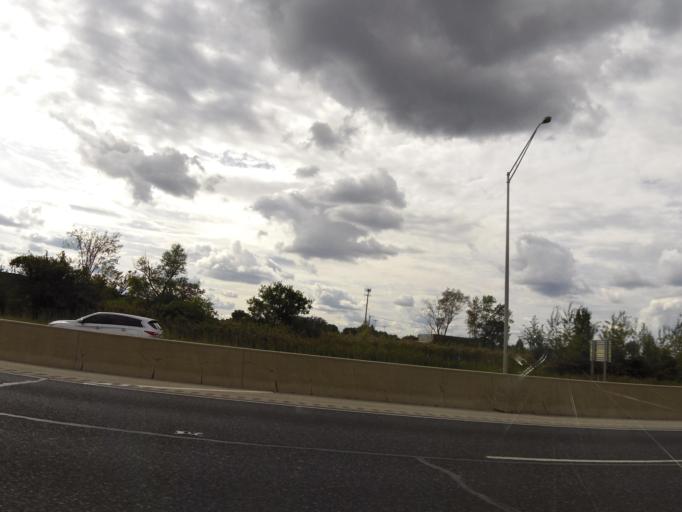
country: US
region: Illinois
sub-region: DuPage County
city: Woodridge
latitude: 41.7293
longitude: -88.0347
